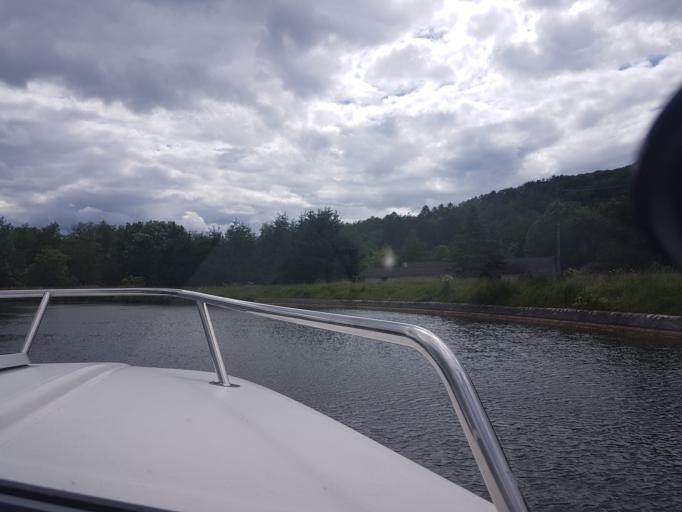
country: FR
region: Bourgogne
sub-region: Departement de l'Yonne
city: Vermenton
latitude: 47.5919
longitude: 3.6366
